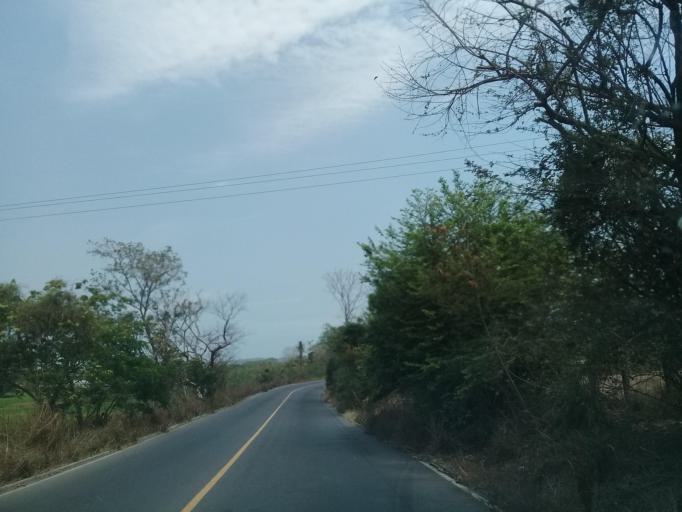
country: MX
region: Veracruz
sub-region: Veracruz
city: Delfino Victoria (Santa Fe)
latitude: 19.1668
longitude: -96.2869
